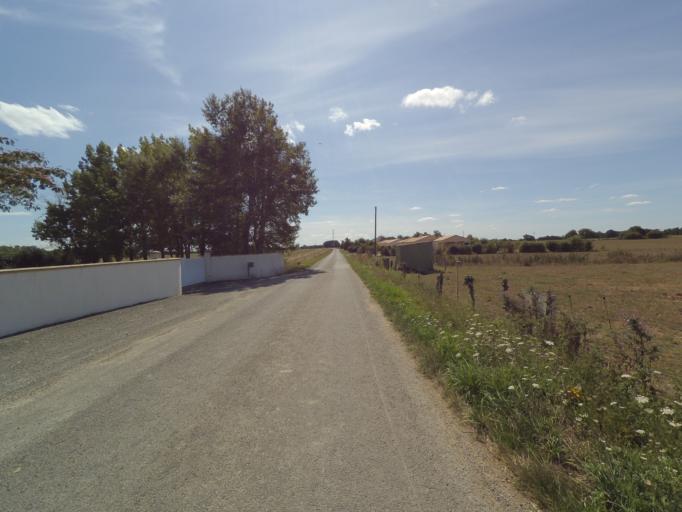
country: FR
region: Pays de la Loire
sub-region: Departement de la Vendee
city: Bouffere
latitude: 46.9816
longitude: -1.3825
